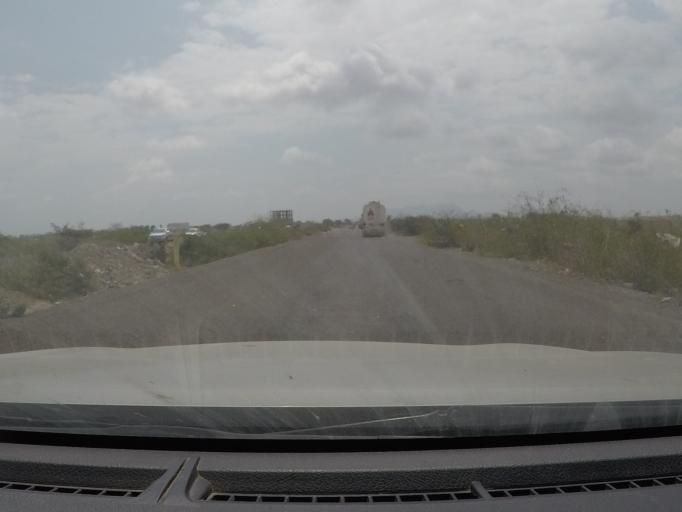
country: YE
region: Aden
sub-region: Ash Shaikh Outhman
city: Ash Shaykh `Uthman
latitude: 12.9097
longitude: 45.0100
